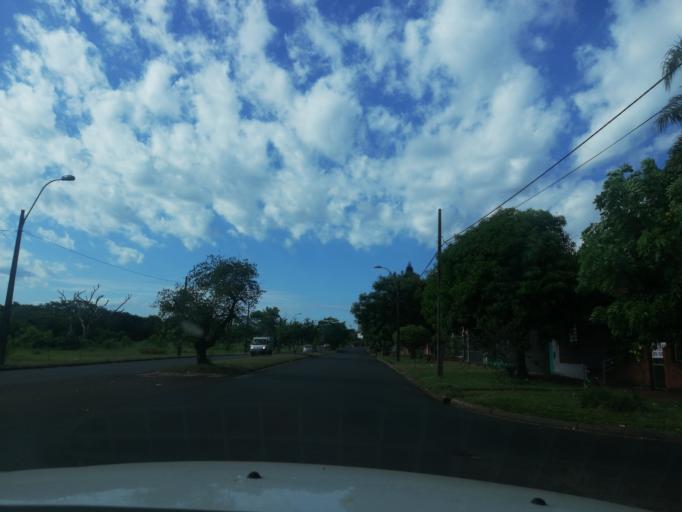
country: PY
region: Itapua
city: Encarnacion
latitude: -27.3507
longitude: -55.8490
